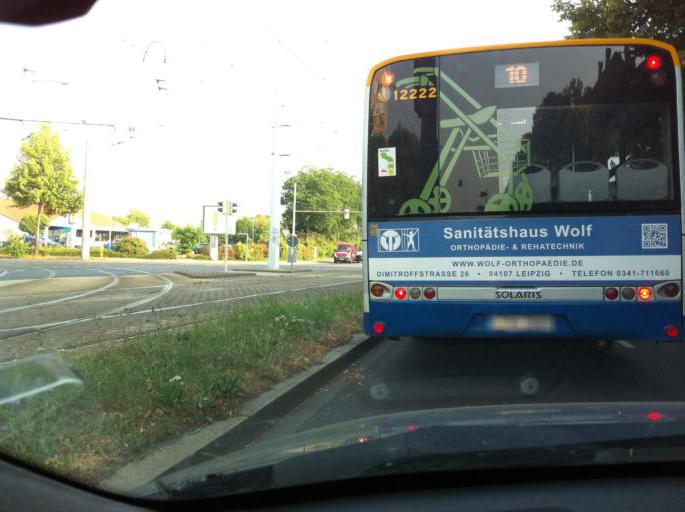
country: DE
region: Saxony
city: Leipzig
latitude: 51.3098
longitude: 12.3964
